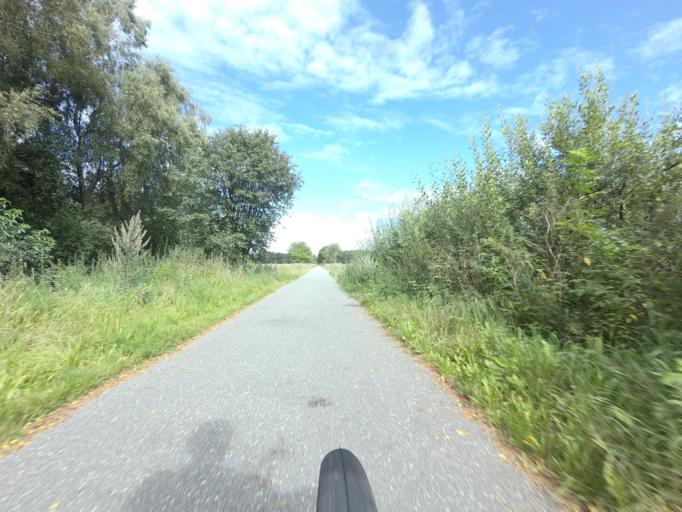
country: DK
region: Central Jutland
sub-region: Norddjurs Kommune
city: Auning
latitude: 56.4374
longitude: 10.3707
